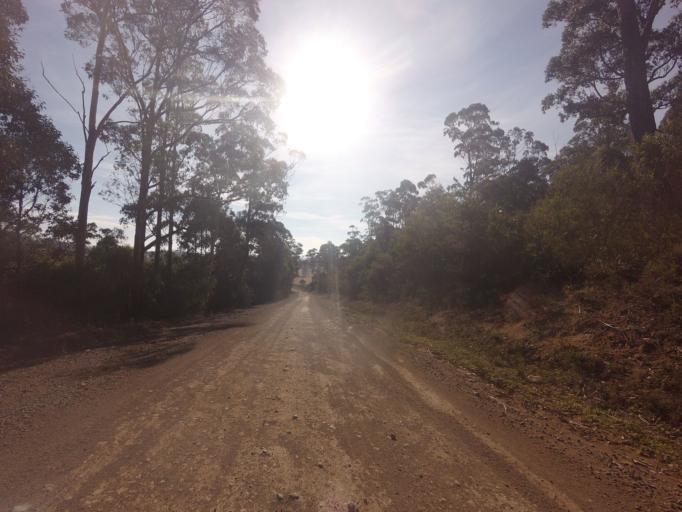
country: AU
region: Tasmania
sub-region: Sorell
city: Sorell
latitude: -42.4822
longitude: 147.4868
